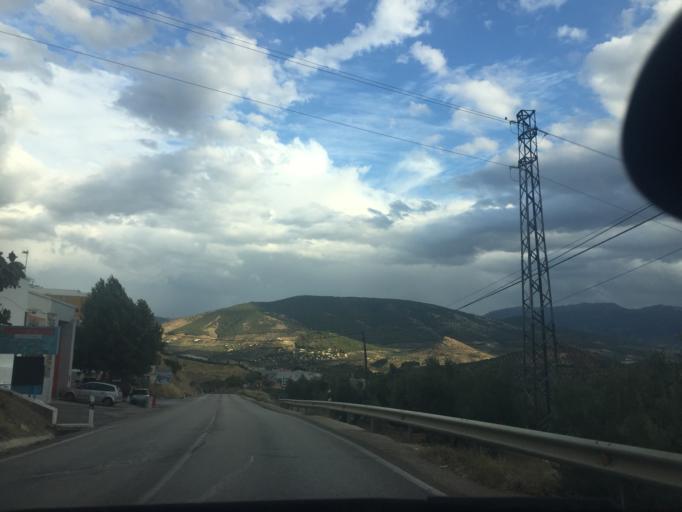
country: ES
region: Andalusia
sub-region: Provincia de Jaen
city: Jaen
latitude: 37.7647
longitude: -3.7720
